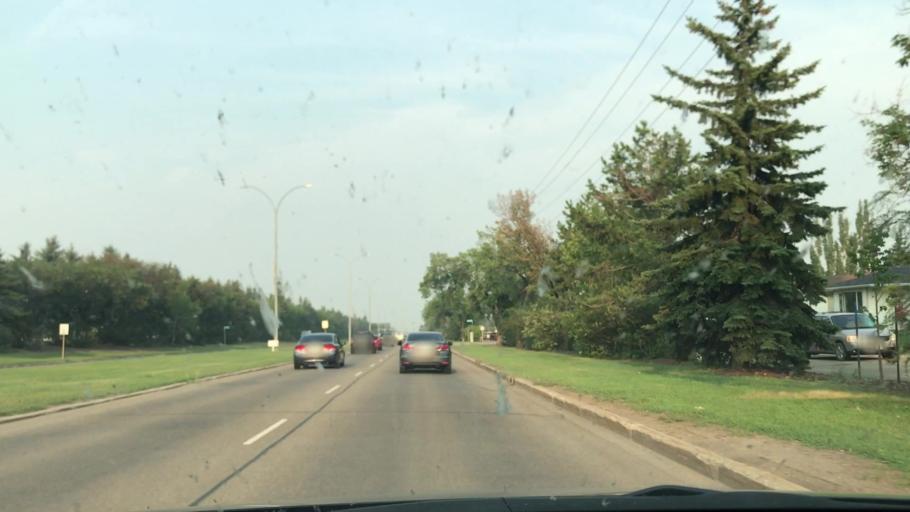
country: CA
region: Alberta
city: Edmonton
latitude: 53.5996
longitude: -113.4642
